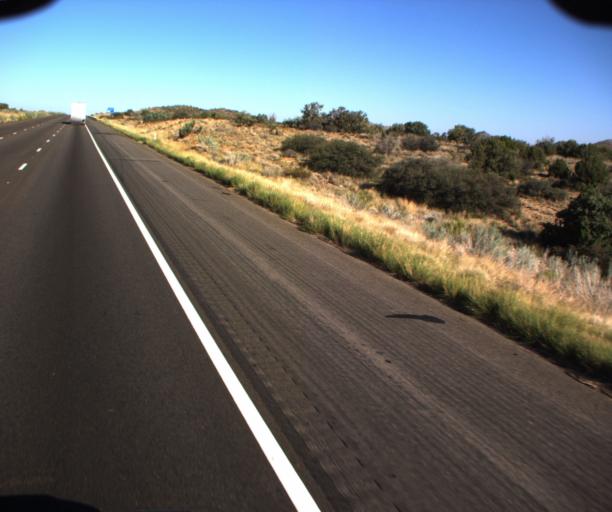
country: US
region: Arizona
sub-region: Mohave County
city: New Kingman-Butler
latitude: 35.1684
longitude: -113.7555
